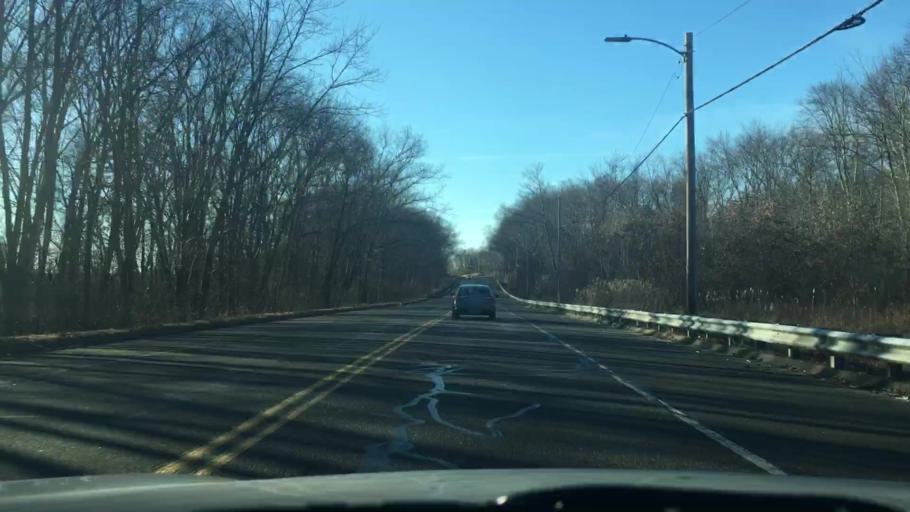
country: US
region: Massachusetts
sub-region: Hampden County
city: Ludlow
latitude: 42.1624
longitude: -72.5176
